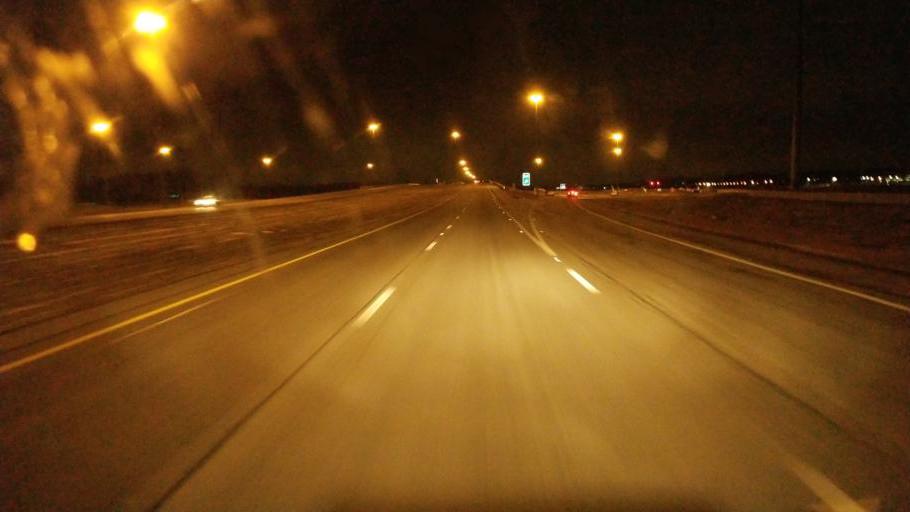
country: US
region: Ohio
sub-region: Franklin County
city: New Albany
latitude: 40.0807
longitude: -82.7482
